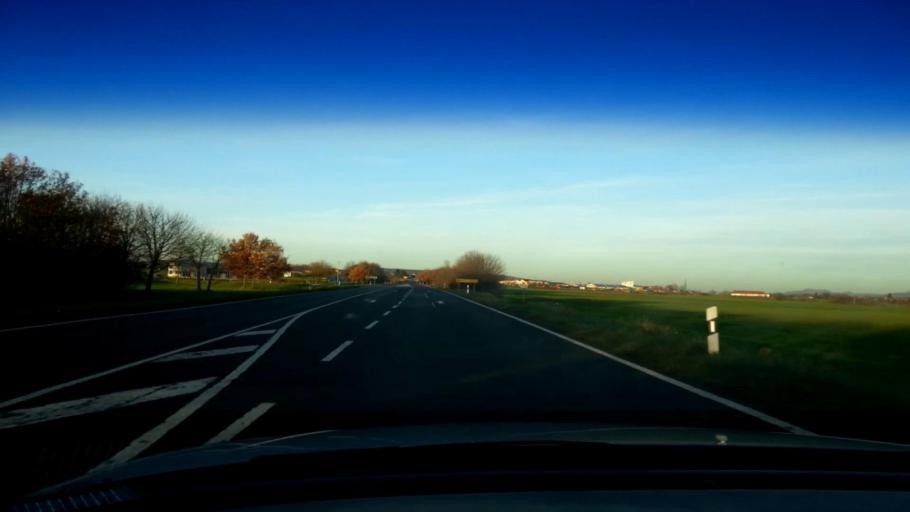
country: DE
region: Bavaria
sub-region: Upper Franconia
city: Rattelsdorf
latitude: 50.0038
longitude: 10.8880
